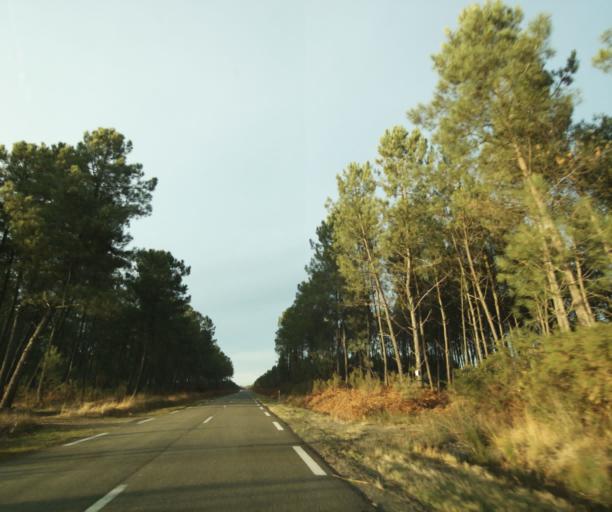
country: FR
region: Aquitaine
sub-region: Departement des Landes
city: Roquefort
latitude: 44.1770
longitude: -0.1437
